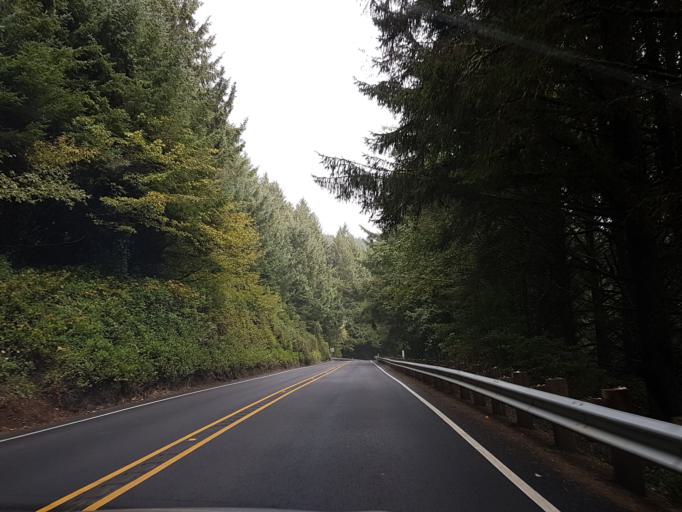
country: US
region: Oregon
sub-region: Lane County
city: Florence
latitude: 44.1202
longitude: -124.1238
